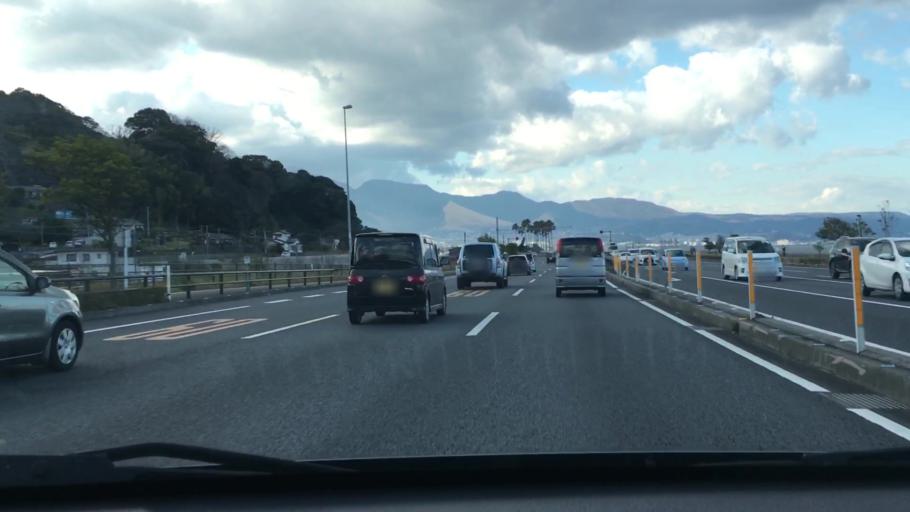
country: JP
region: Oita
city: Oita
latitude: 33.2536
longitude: 131.5638
